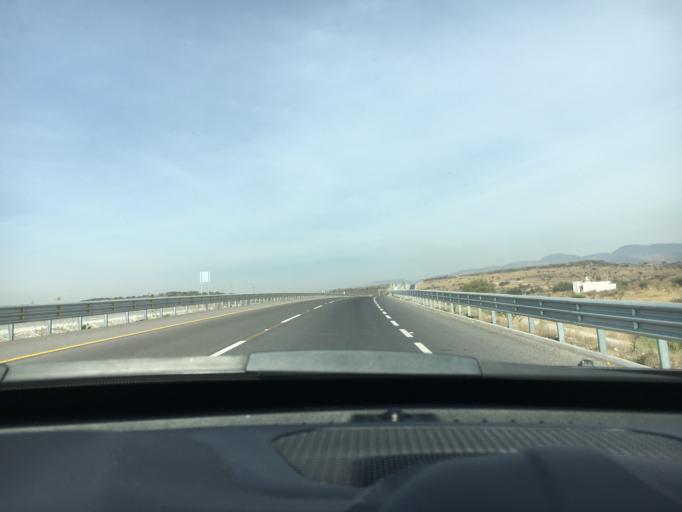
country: MX
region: Guanajuato
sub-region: Silao de la Victoria
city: El Refugio de los Sauces
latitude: 21.0498
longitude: -101.5279
